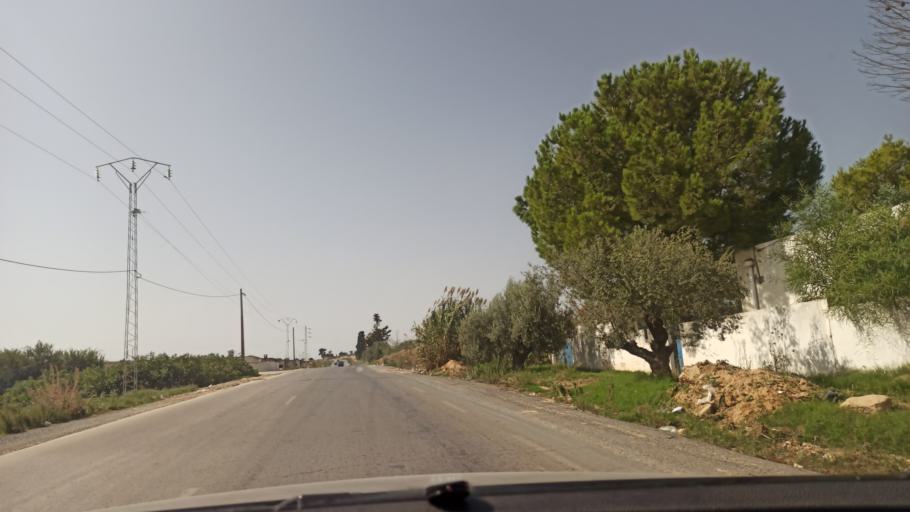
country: TN
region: Manouba
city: Manouba
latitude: 36.7428
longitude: 10.0906
